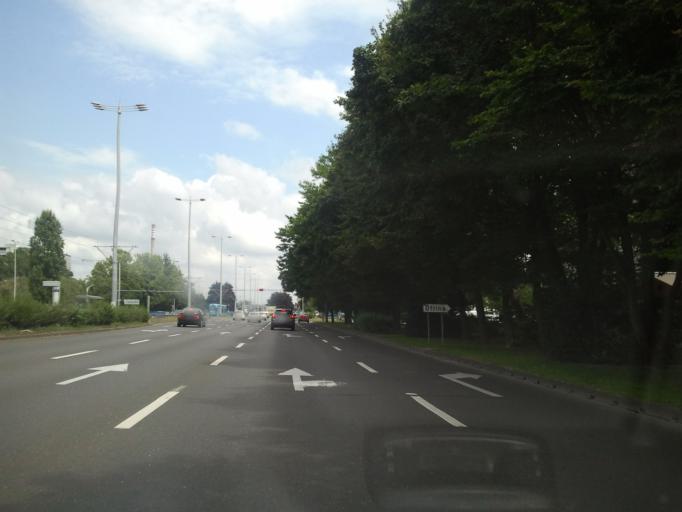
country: HR
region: Grad Zagreb
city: Novi Zagreb
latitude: 45.7779
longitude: 15.9947
